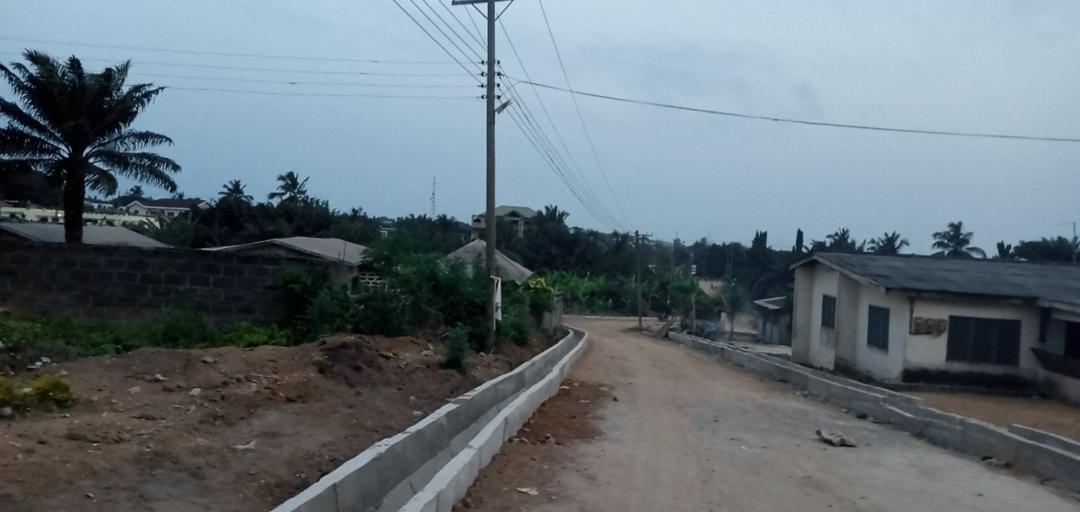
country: GH
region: Central
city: Winneba
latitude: 5.3568
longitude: -0.6265
